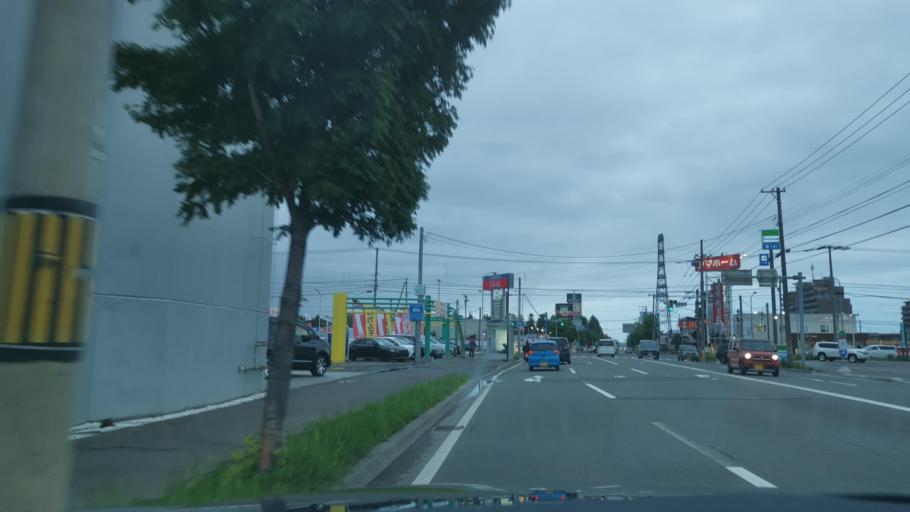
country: JP
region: Hokkaido
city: Sapporo
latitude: 43.1087
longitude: 141.2790
